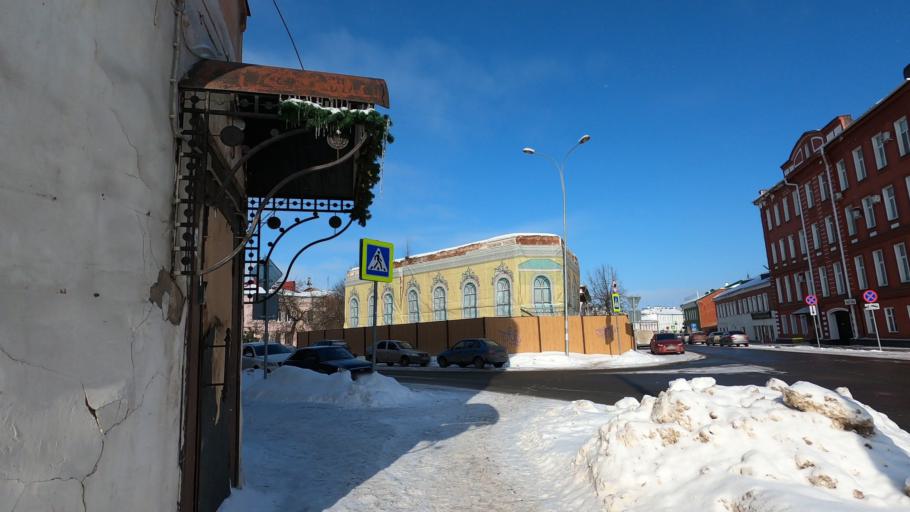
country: RU
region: Jaroslavl
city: Rybinsk
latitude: 58.0477
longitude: 38.8525
